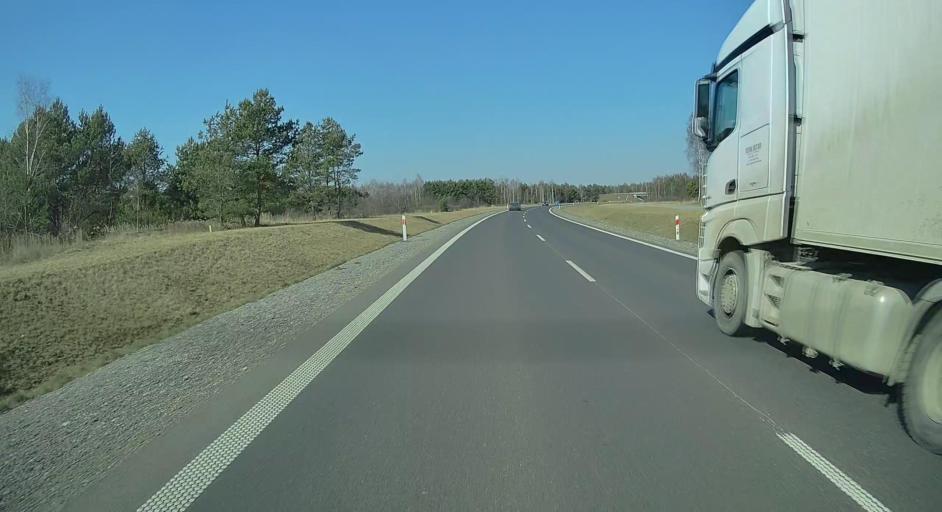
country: PL
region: Subcarpathian Voivodeship
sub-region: Powiat nizanski
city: Raclawice
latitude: 50.4972
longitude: 22.1802
